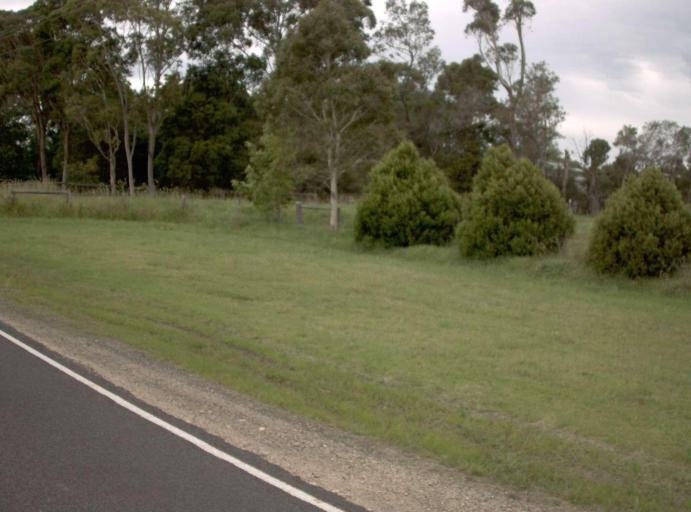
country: AU
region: Victoria
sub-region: Wellington
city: Sale
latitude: -38.0709
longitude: 147.0975
